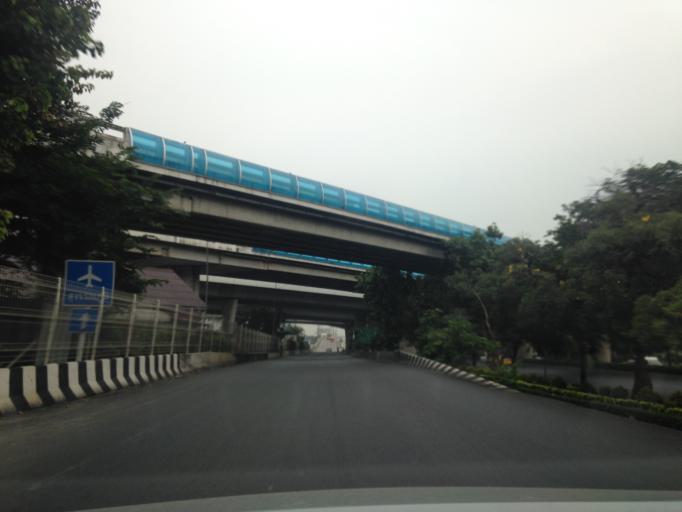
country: TH
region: Bangkok
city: Khan Na Yao
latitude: 13.8284
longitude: 100.6734
